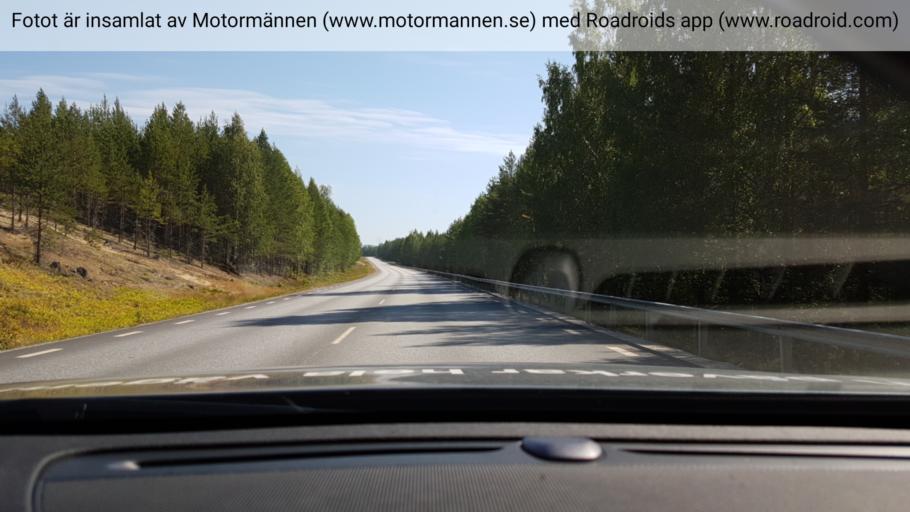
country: SE
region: Vaesterbotten
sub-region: Vindelns Kommun
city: Vindeln
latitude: 64.1502
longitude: 19.8604
